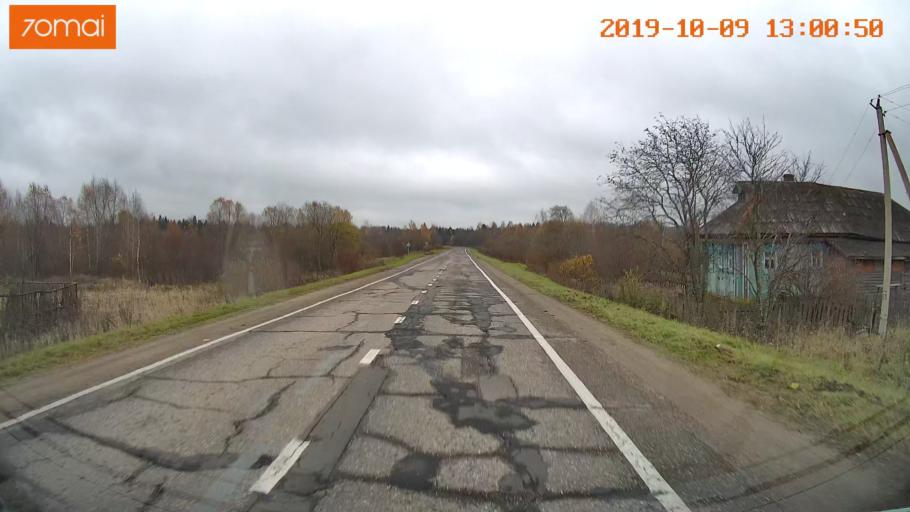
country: RU
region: Jaroslavl
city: Prechistoye
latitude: 58.3737
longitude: 40.4830
